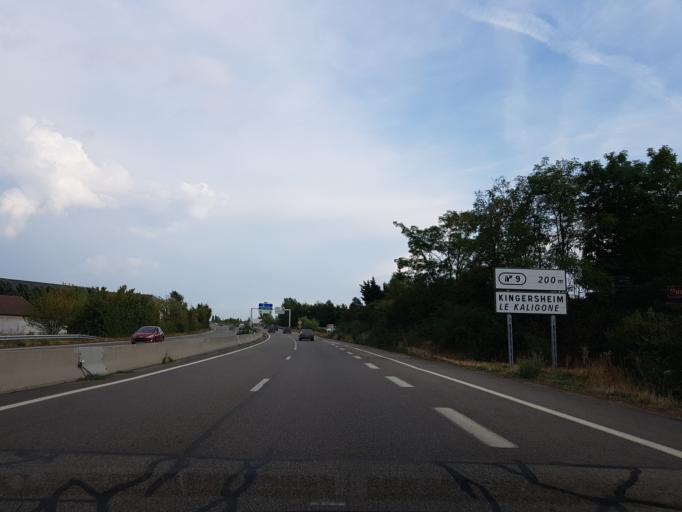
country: FR
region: Alsace
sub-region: Departement du Haut-Rhin
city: Kingersheim
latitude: 47.7937
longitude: 7.3114
